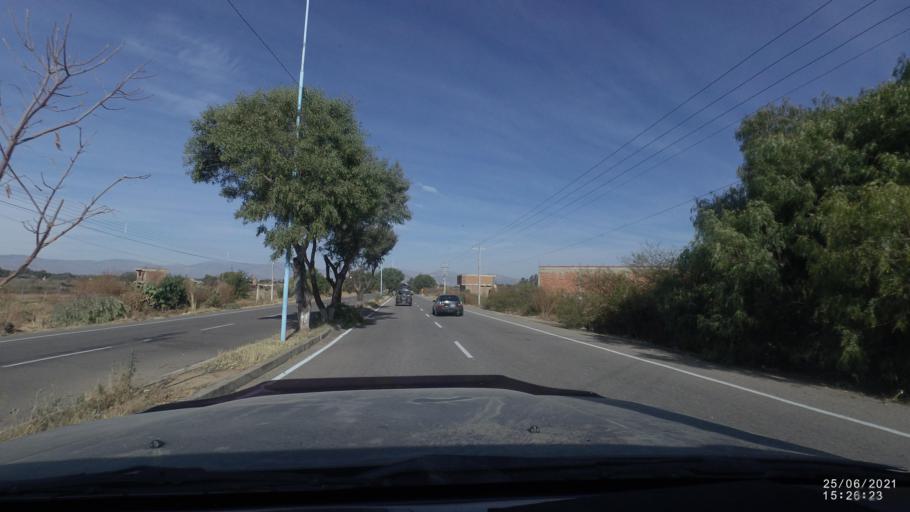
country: BO
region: Cochabamba
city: Cliza
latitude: -17.5383
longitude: -65.9600
